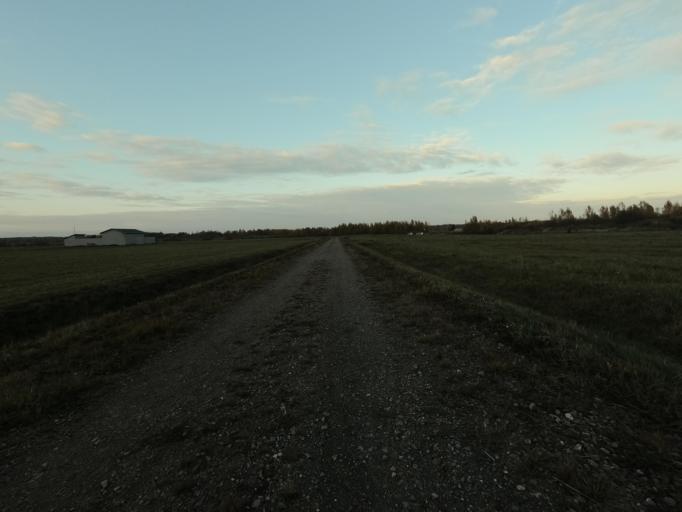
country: RU
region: Leningrad
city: Mga
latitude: 59.7881
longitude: 31.1997
